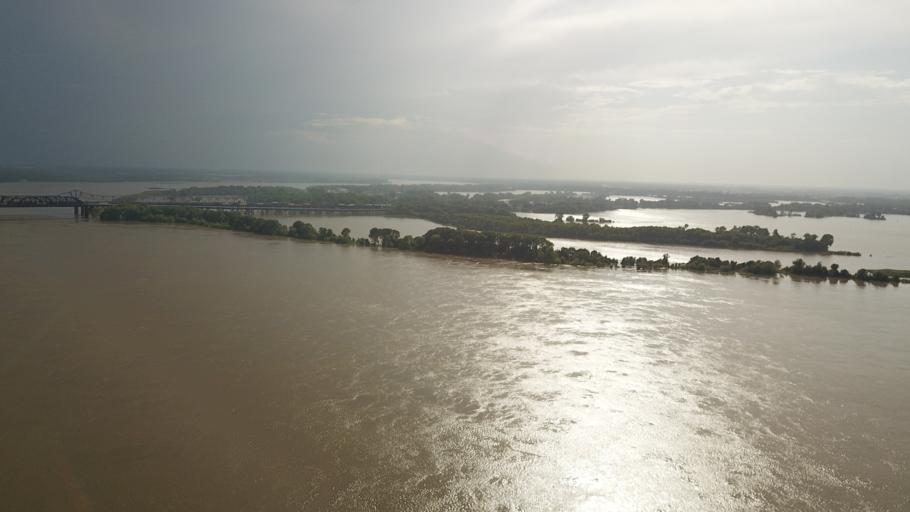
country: US
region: Tennessee
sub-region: Shelby County
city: Memphis
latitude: 35.1395
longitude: -90.0631
